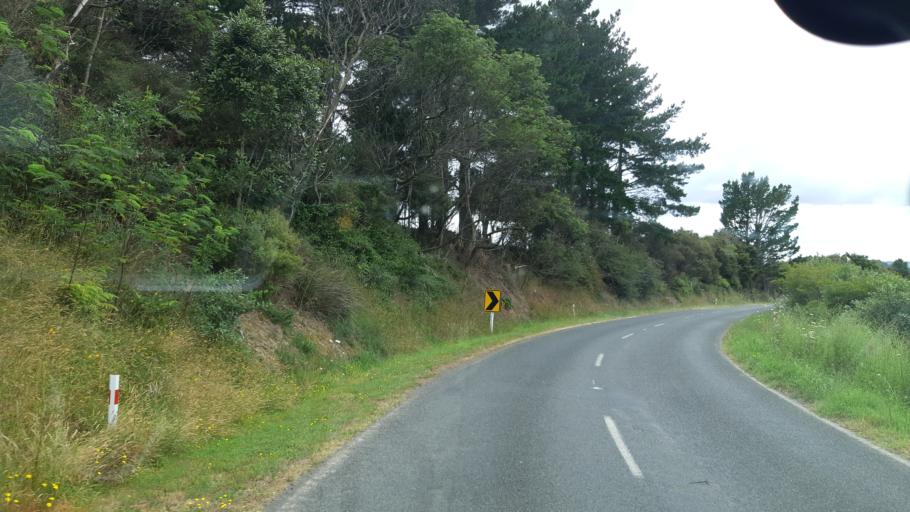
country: NZ
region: Waikato
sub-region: Waikato District
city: Ngaruawahia
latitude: -37.5611
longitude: 175.0626
